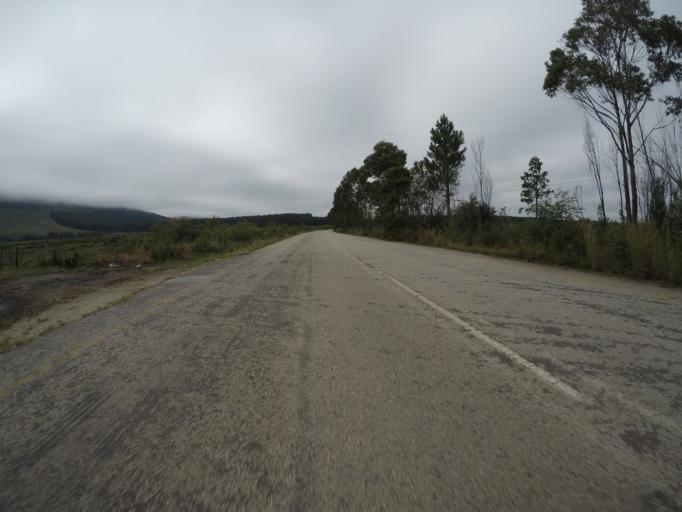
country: ZA
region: Eastern Cape
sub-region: Cacadu District Municipality
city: Kareedouw
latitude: -33.9985
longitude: 24.1729
